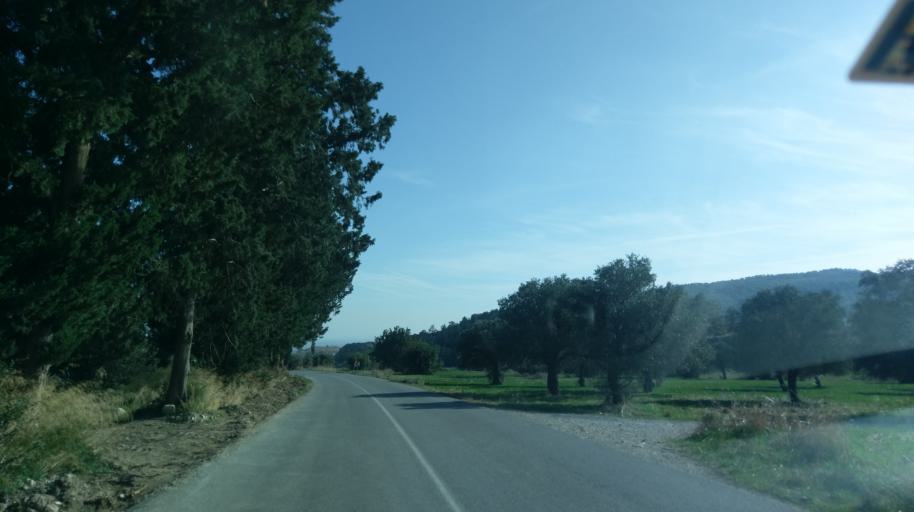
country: CY
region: Ammochostos
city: Trikomo
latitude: 35.3399
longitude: 33.8040
